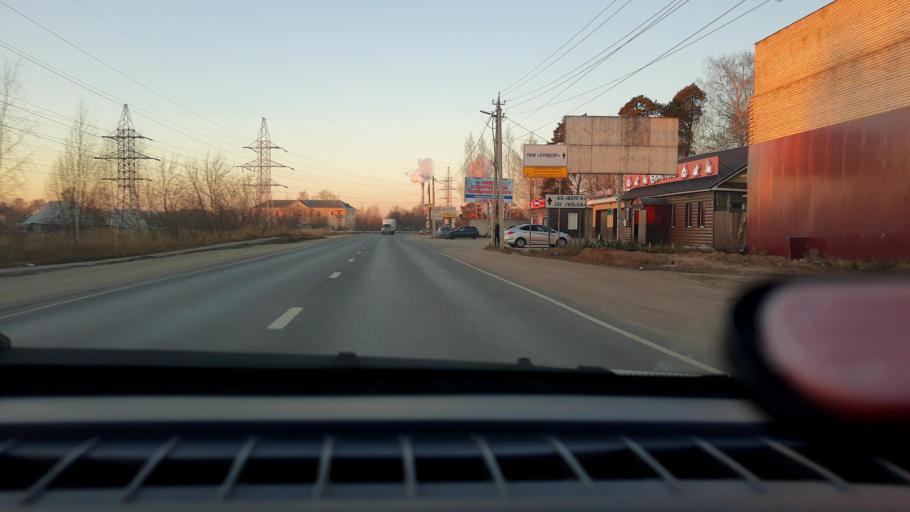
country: RU
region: Nizjnij Novgorod
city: Novaya Balakhna
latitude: 56.4854
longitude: 43.5985
